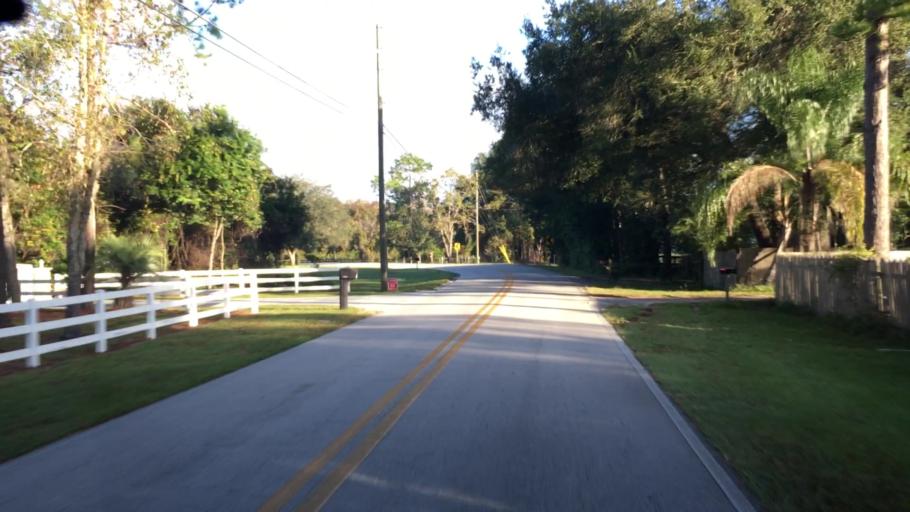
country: US
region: Florida
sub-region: Volusia County
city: North DeLand
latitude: 29.0725
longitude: -81.2713
